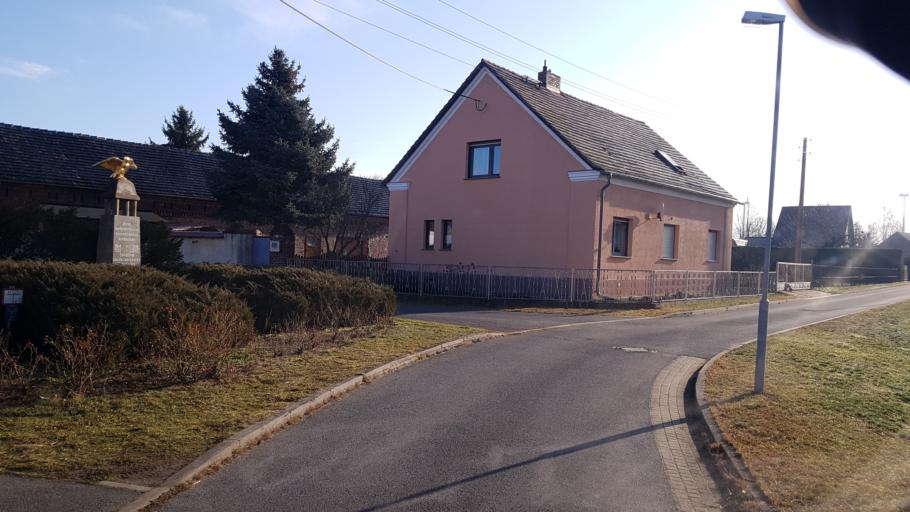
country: DE
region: Brandenburg
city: Lubbenau
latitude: 51.8175
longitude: 13.9043
